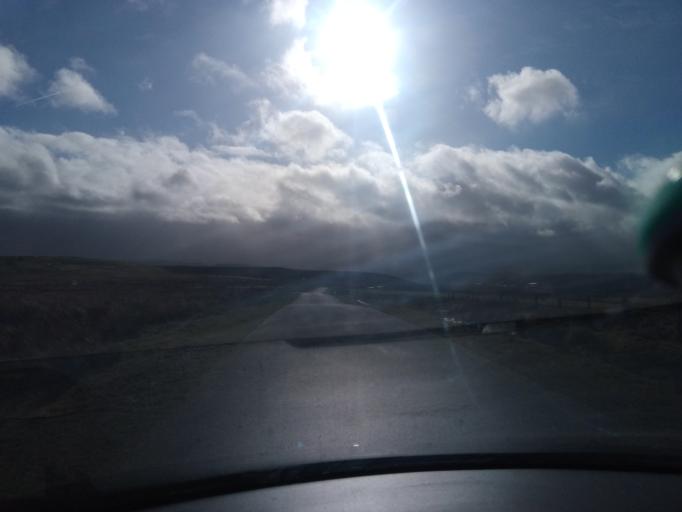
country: GB
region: England
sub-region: Northumberland
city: Rochester
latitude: 55.3383
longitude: -2.2882
